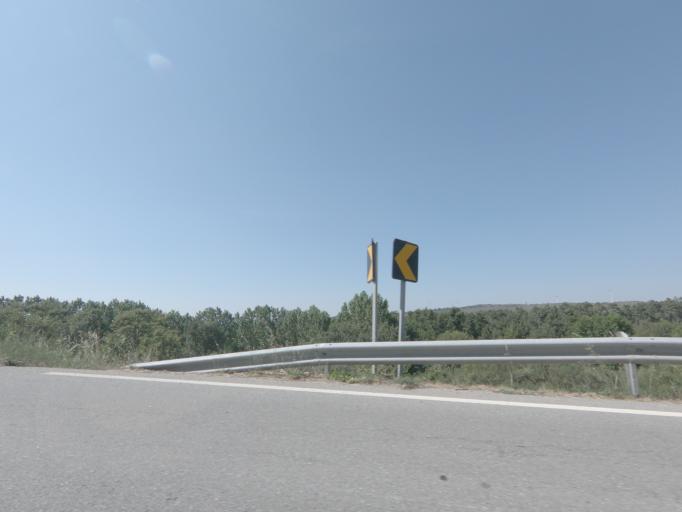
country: PT
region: Viseu
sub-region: Moimenta da Beira
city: Moimenta da Beira
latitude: 41.0080
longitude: -7.6846
